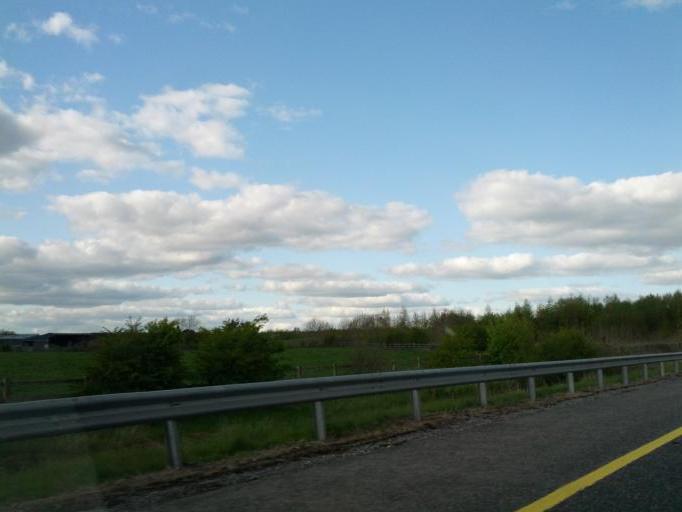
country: IE
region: Leinster
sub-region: An Iarmhi
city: Rochfortbridge
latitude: 53.4099
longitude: -7.2737
